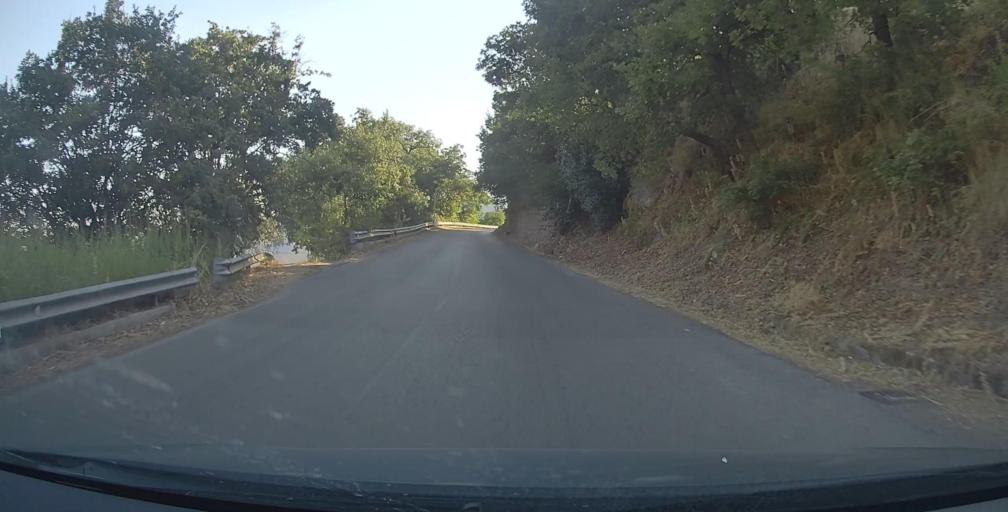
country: IT
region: Sicily
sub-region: Messina
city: San Piero Patti
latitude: 38.0772
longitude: 14.9793
